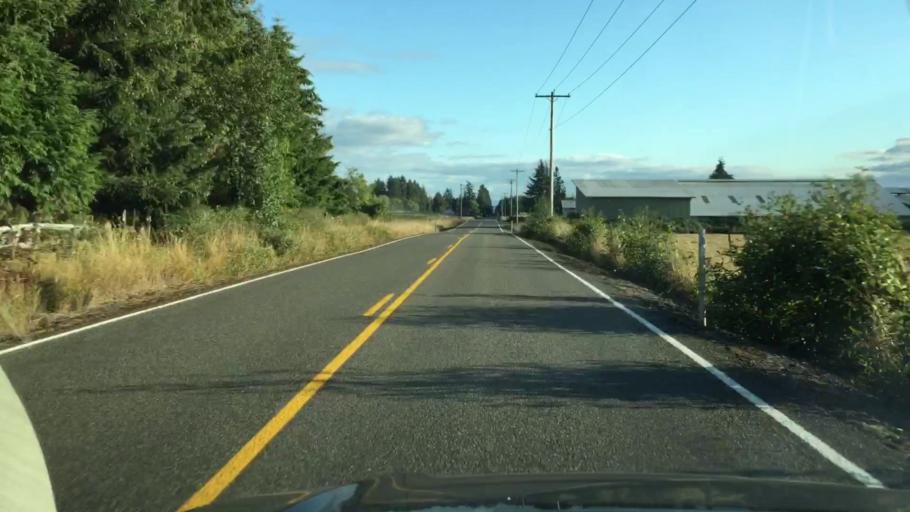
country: US
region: Washington
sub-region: Lewis County
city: Napavine
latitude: 46.5241
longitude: -122.7405
